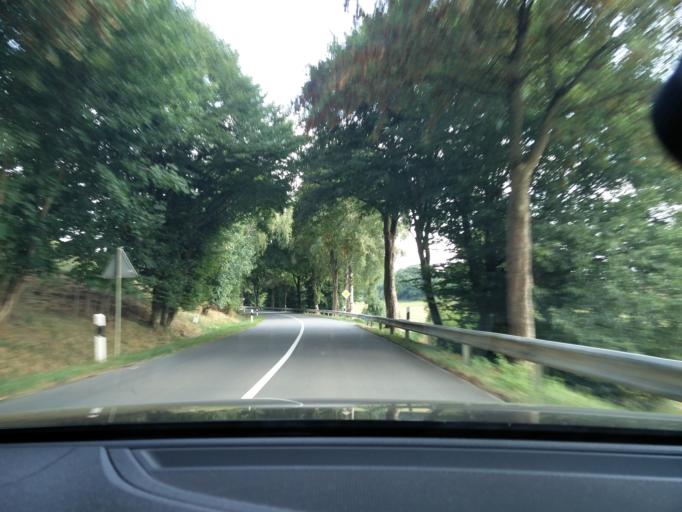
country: DE
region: North Rhine-Westphalia
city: Lichtenau
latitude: 51.6785
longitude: 8.9116
